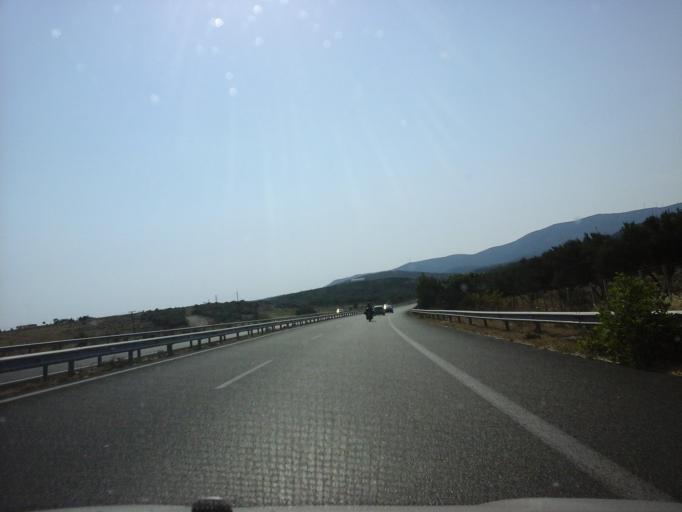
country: GR
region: East Macedonia and Thrace
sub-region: Nomos Evrou
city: Alexandroupoli
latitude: 40.8667
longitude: 25.8250
